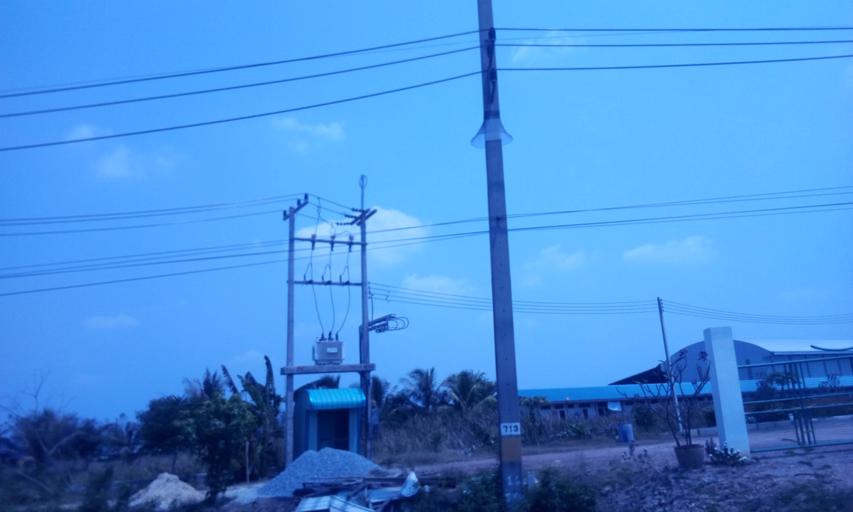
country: TH
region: Chachoengsao
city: Bang Nam Priao
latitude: 13.8340
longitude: 101.0553
